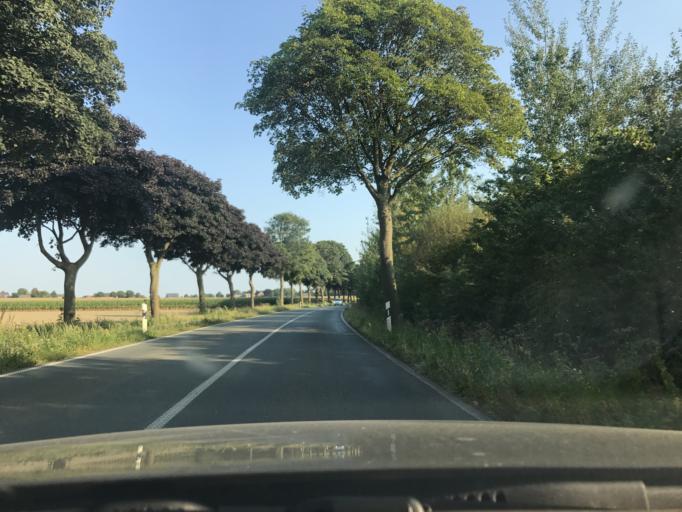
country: DE
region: North Rhine-Westphalia
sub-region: Regierungsbezirk Dusseldorf
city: Kleve
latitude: 51.7480
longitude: 6.1922
